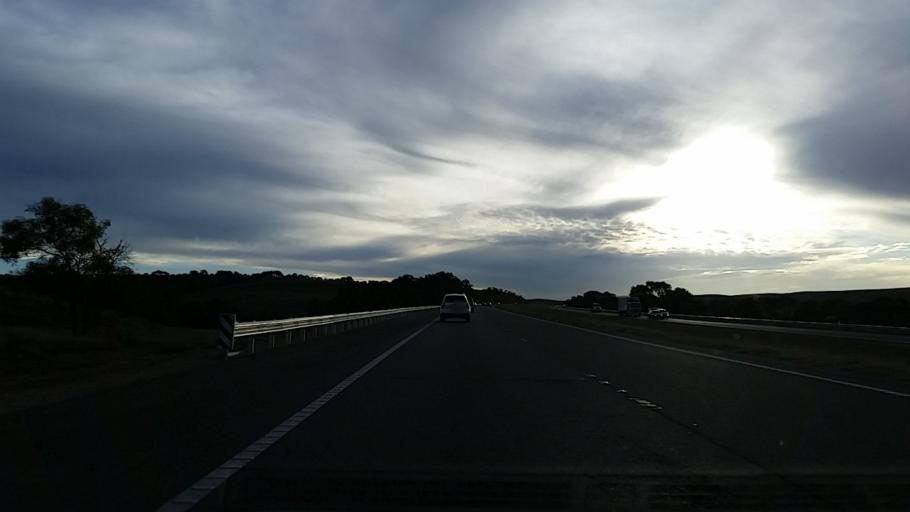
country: AU
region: South Australia
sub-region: Mount Barker
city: Callington
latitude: -35.1224
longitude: 139.0236
